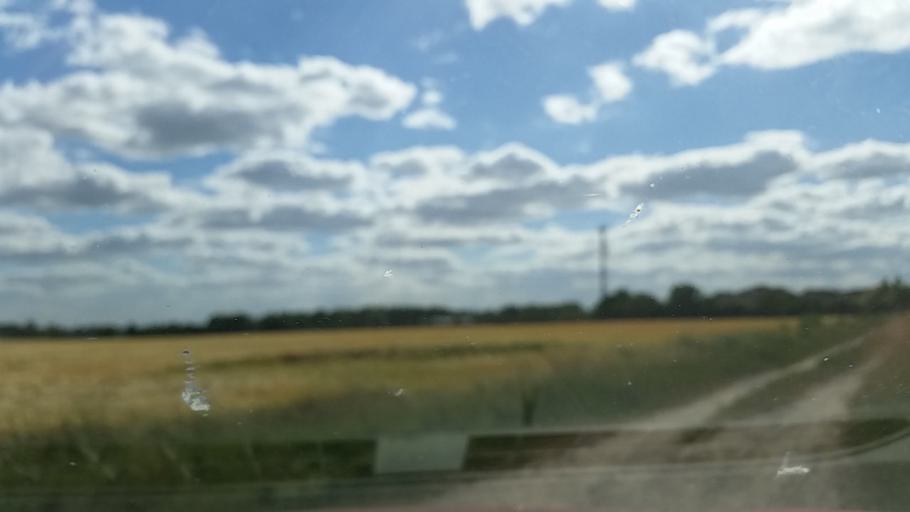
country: DE
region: Lower Saxony
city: Tappenbeck
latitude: 52.4715
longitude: 10.7280
